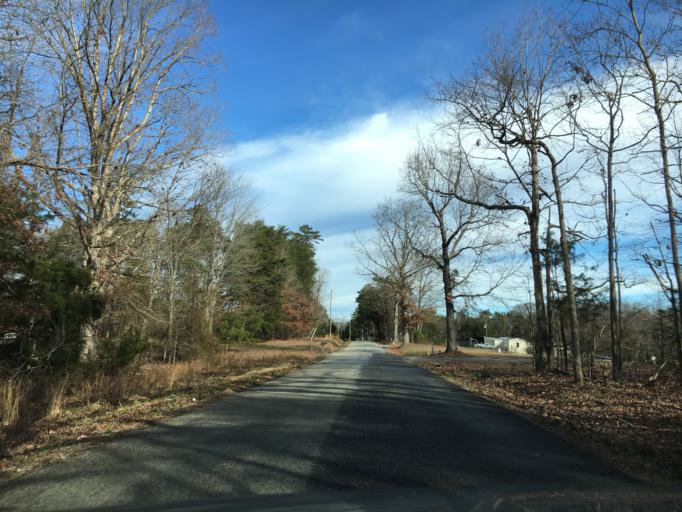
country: US
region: Virginia
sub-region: Nottoway County
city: Crewe
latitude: 37.2613
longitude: -78.2232
